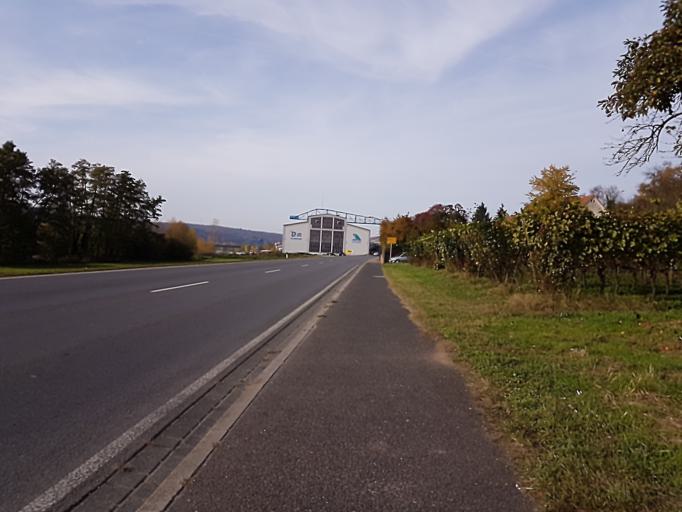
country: DE
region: Bavaria
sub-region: Regierungsbezirk Unterfranken
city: Erlenbach am Main
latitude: 49.7960
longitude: 9.1660
